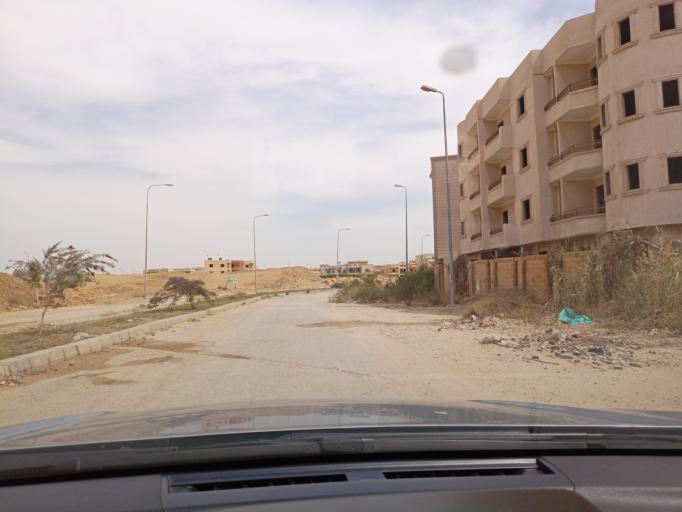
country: EG
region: Muhafazat al Qalyubiyah
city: Al Khankah
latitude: 30.2514
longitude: 31.5023
